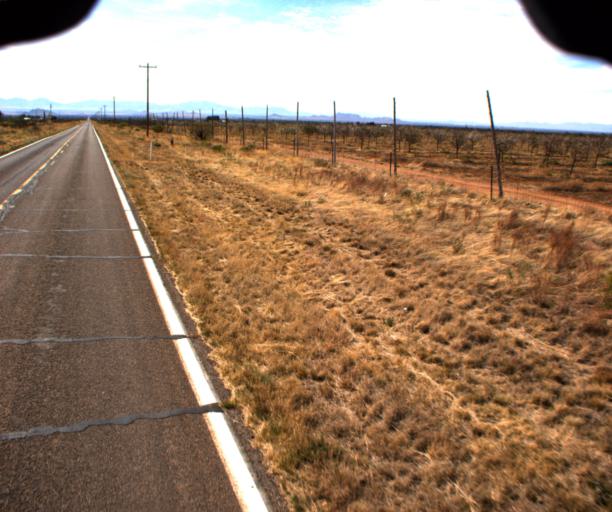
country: US
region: Arizona
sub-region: Cochise County
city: Willcox
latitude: 31.8760
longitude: -109.4931
